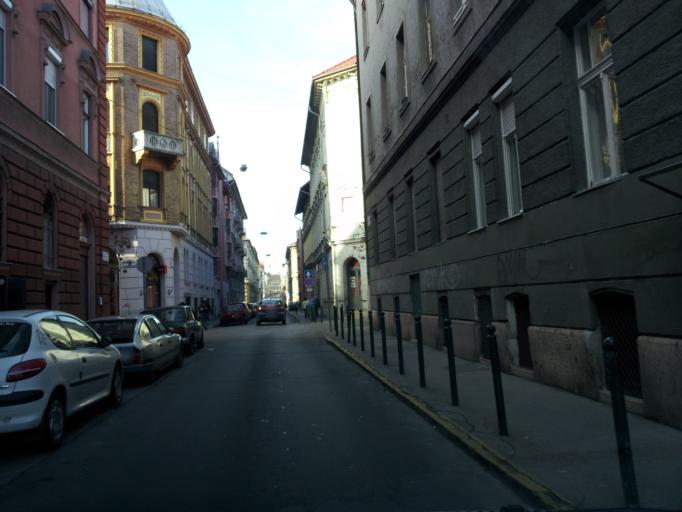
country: HU
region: Budapest
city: Budapest VIII. keruelet
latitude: 47.4825
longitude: 19.0754
